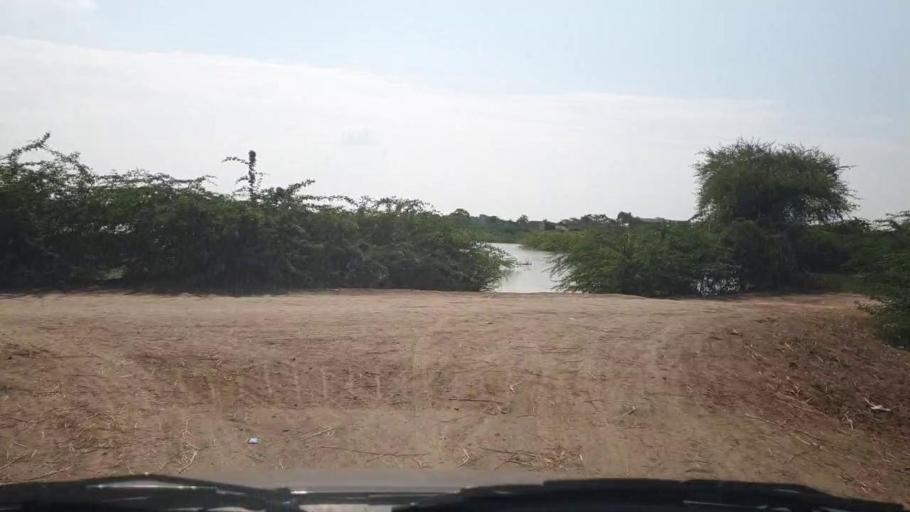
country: PK
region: Sindh
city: Badin
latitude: 24.4794
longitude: 68.6127
